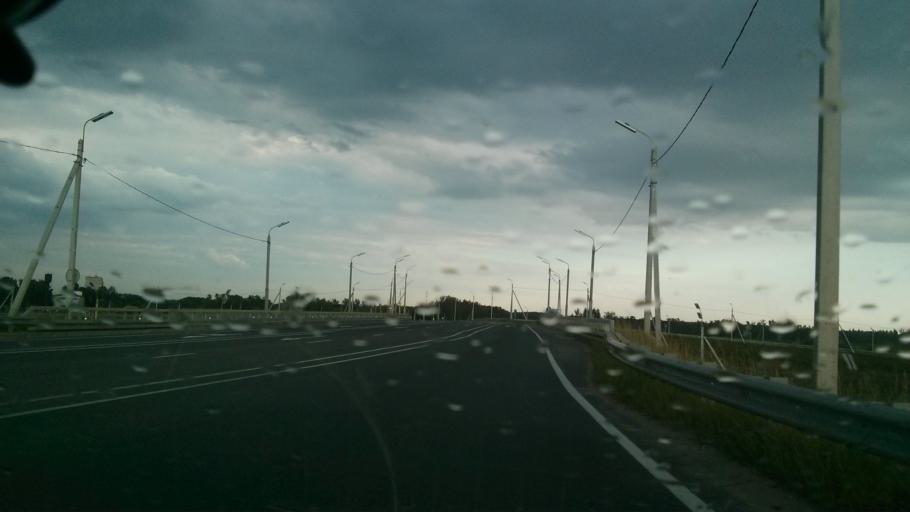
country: RU
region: Vladimir
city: Murom
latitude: 55.6193
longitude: 42.0243
